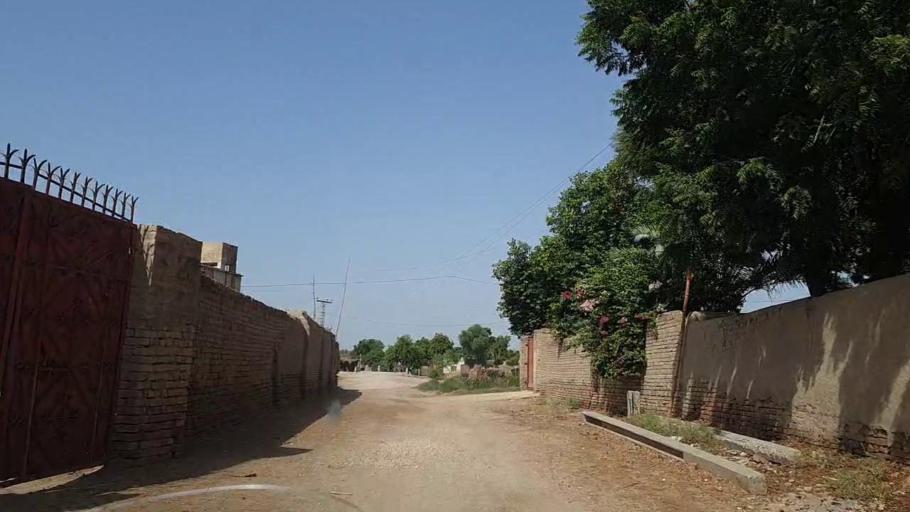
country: PK
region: Sindh
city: Naushahro Firoz
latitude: 26.8728
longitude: 68.0344
